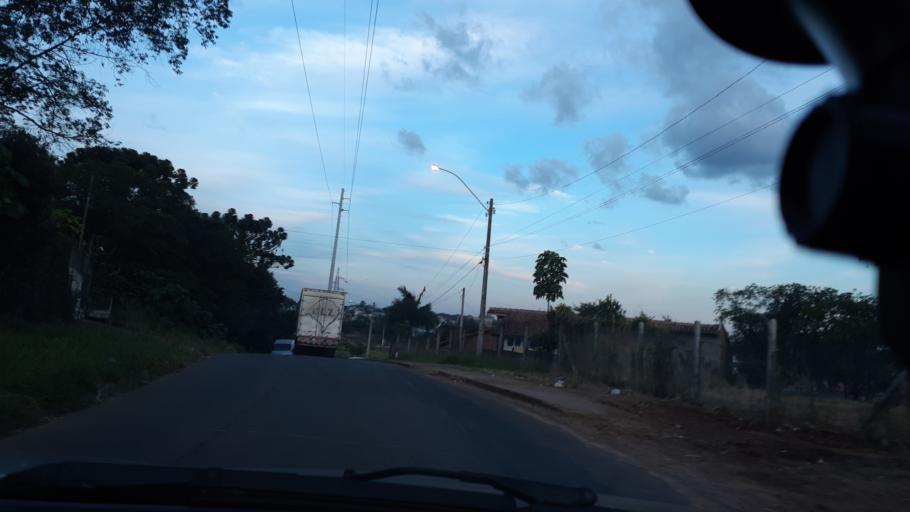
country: BR
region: Rio Grande do Sul
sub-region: Sapucaia Do Sul
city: Sapucaia
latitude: -29.8457
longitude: -51.1474
